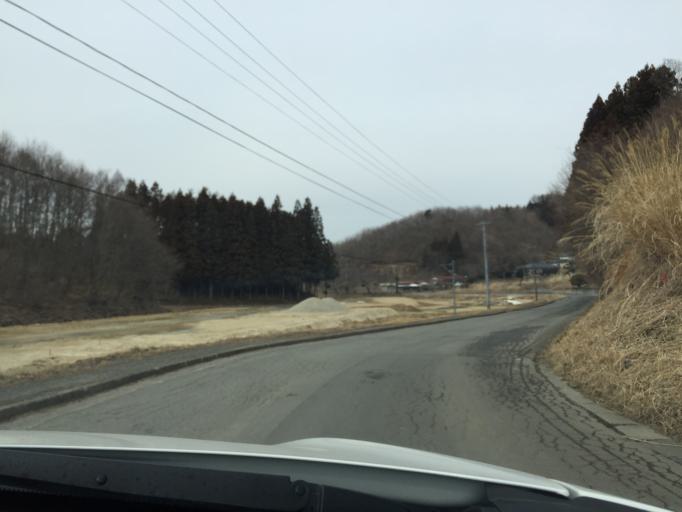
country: JP
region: Fukushima
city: Ishikawa
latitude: 37.1770
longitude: 140.5685
